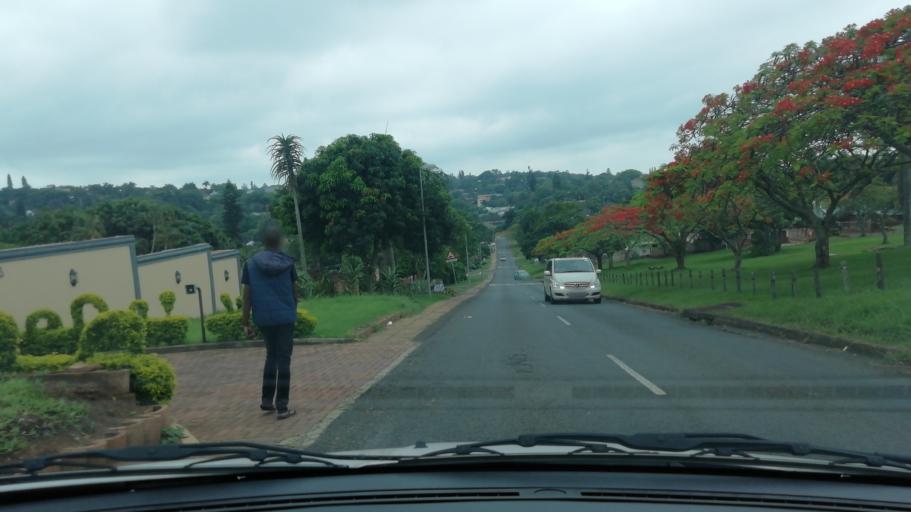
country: ZA
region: KwaZulu-Natal
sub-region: uThungulu District Municipality
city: Empangeni
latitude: -28.7622
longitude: 31.8918
